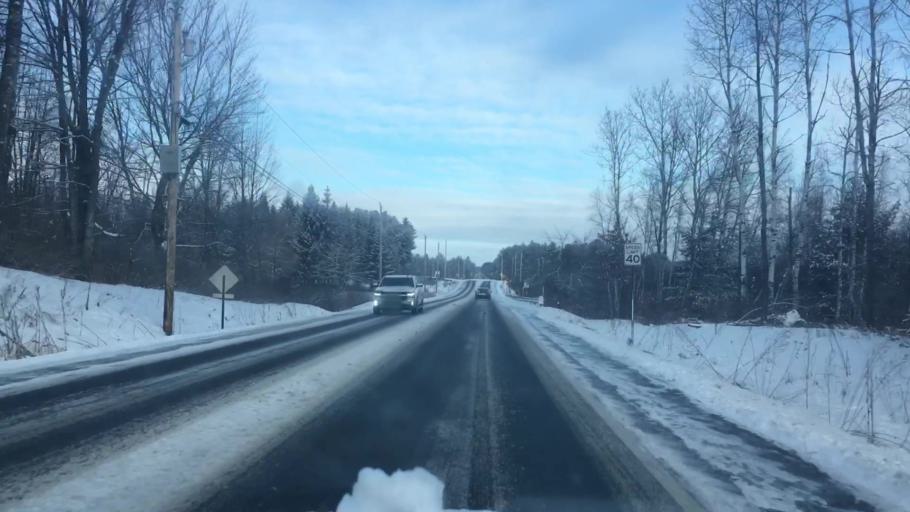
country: US
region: Maine
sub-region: Cumberland County
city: North Windham
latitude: 43.7956
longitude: -70.4400
